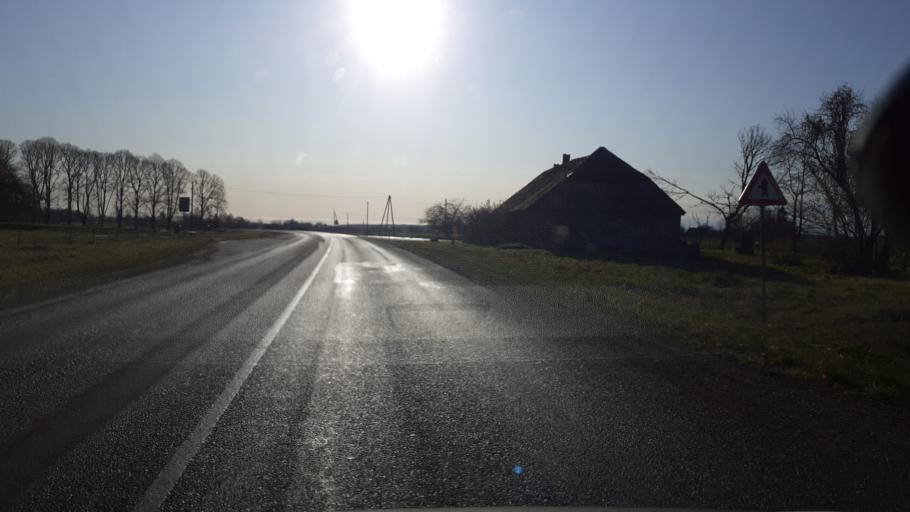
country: LV
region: Kuldigas Rajons
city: Kuldiga
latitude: 57.0122
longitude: 21.8789
